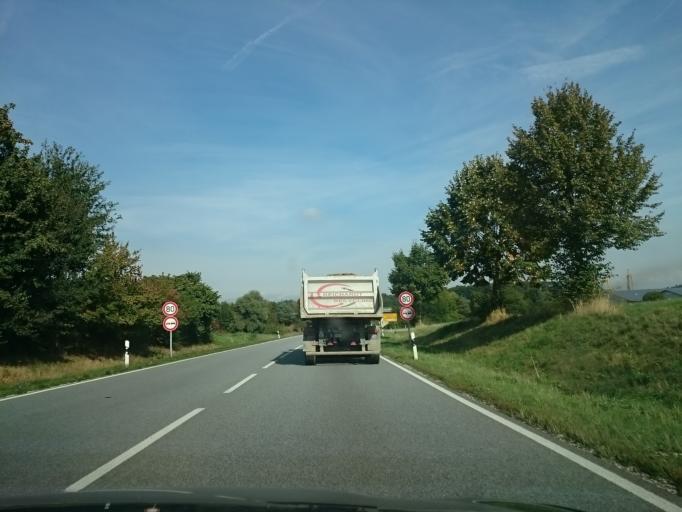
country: DE
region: Bavaria
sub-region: Upper Bavaria
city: Gachenbach
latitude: 48.5271
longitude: 11.2396
